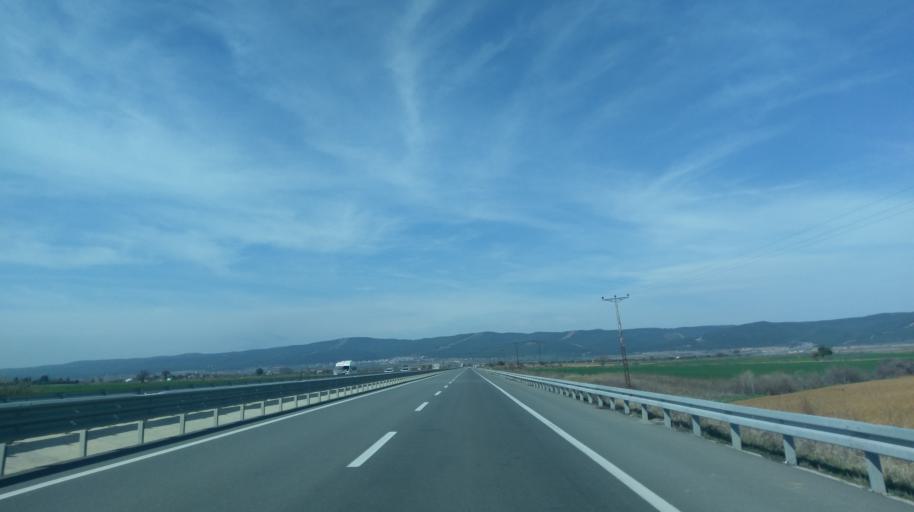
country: TR
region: Canakkale
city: Evrese
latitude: 40.6594
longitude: 26.8165
